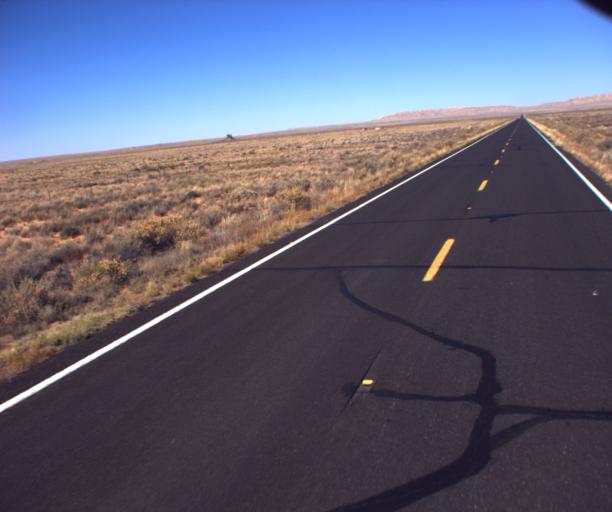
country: US
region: Arizona
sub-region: Navajo County
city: First Mesa
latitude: 35.7015
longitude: -110.5079
